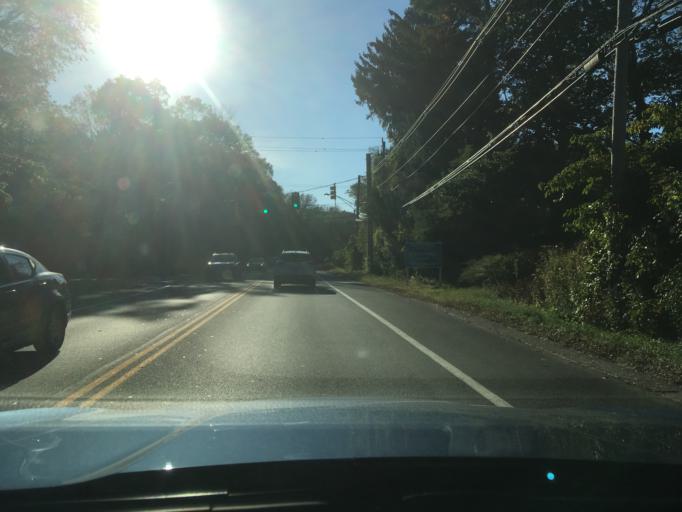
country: US
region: Rhode Island
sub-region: Kent County
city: East Greenwich
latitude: 41.6629
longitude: -71.4772
